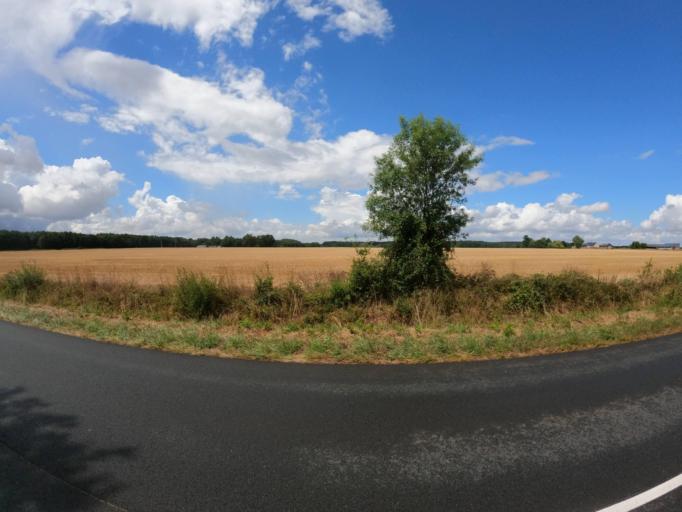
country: FR
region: Pays de la Loire
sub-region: Departement de Maine-et-Loire
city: Feneu
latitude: 47.5883
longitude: -0.5903
